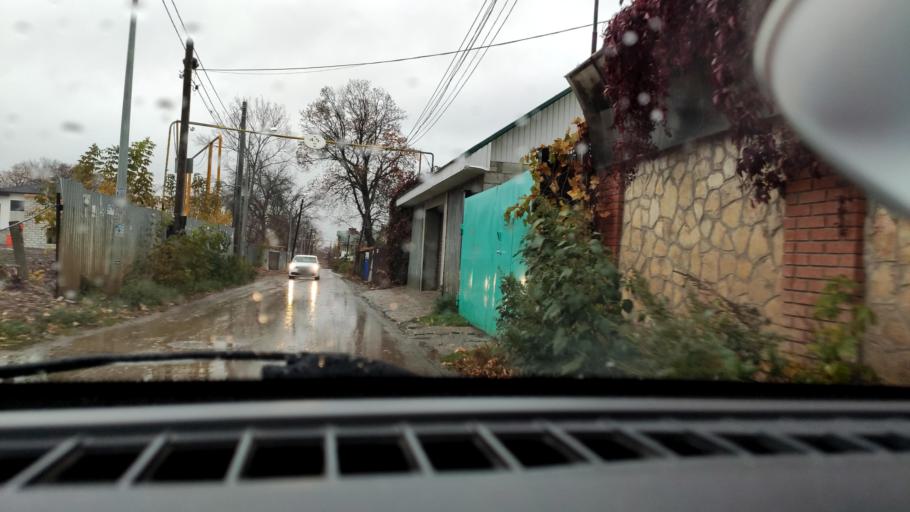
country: RU
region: Samara
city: Samara
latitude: 53.2336
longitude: 50.1743
